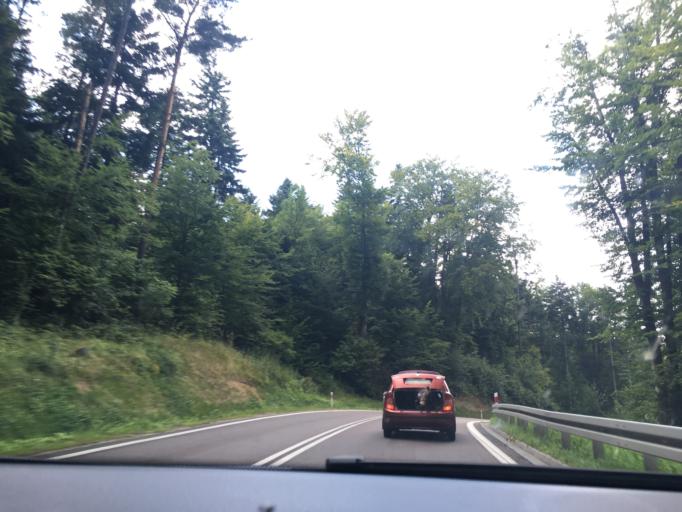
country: PL
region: Subcarpathian Voivodeship
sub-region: Powiat brzozowski
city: Jablonica Polska
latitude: 49.7266
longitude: 21.9080
